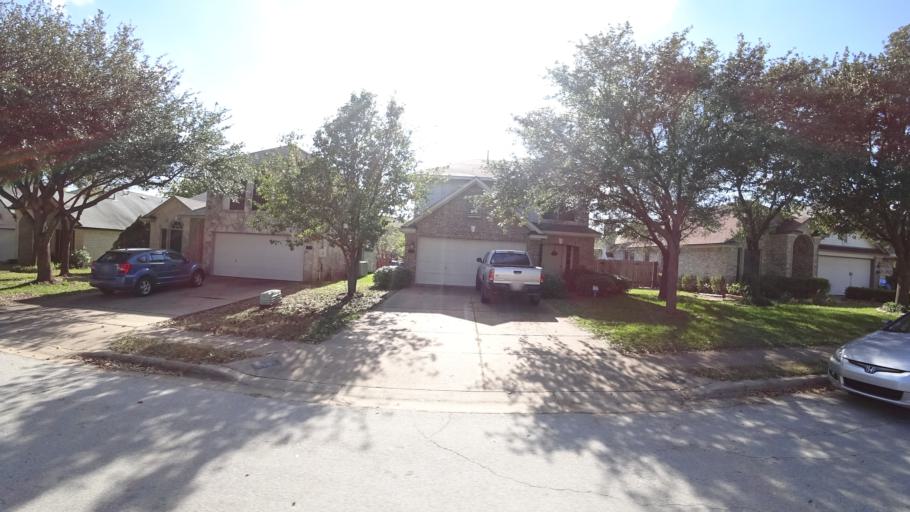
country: US
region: Texas
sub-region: Travis County
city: Wells Branch
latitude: 30.4574
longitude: -97.6846
